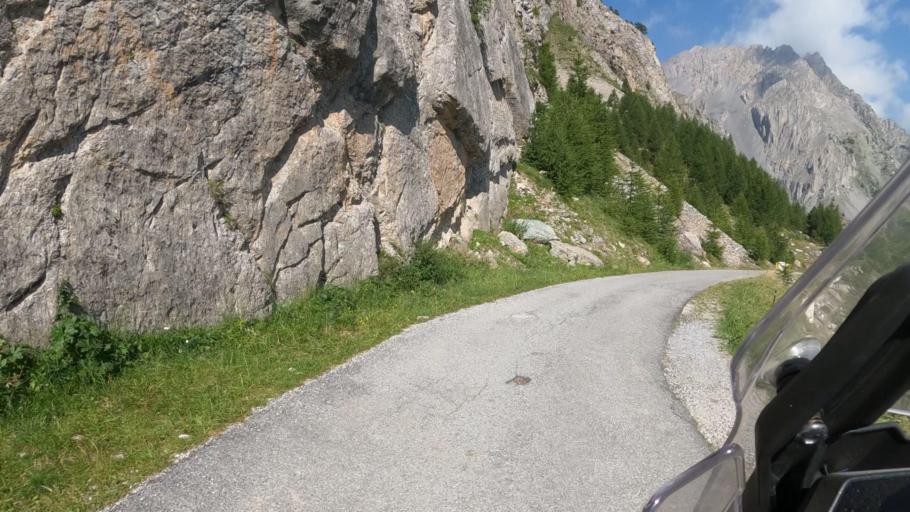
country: IT
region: Piedmont
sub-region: Provincia di Cuneo
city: Pietraporzio
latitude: 44.4051
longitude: 7.0399
